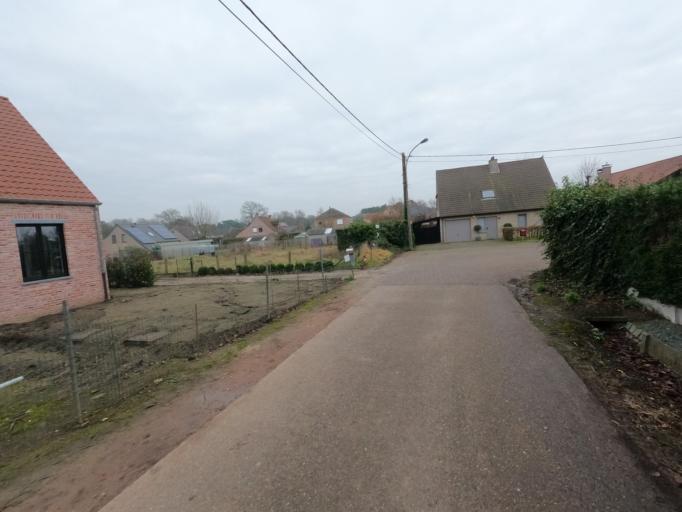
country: BE
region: Flanders
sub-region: Provincie Antwerpen
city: Schilde
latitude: 51.3012
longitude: 4.5780
